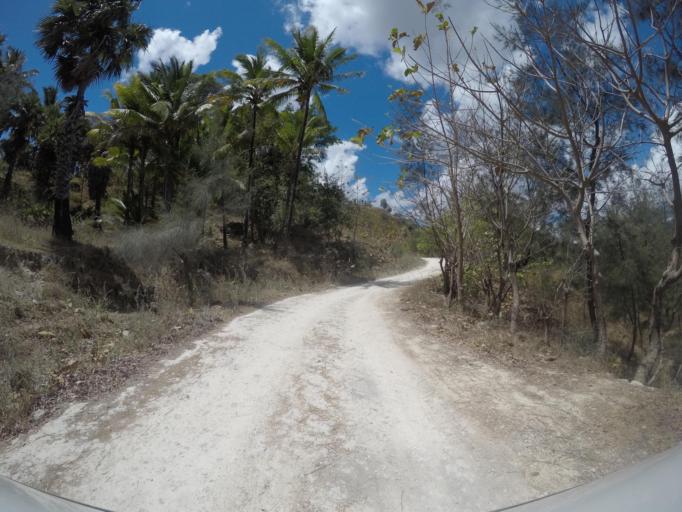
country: TL
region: Baucau
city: Baucau
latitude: -8.4850
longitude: 126.6380
